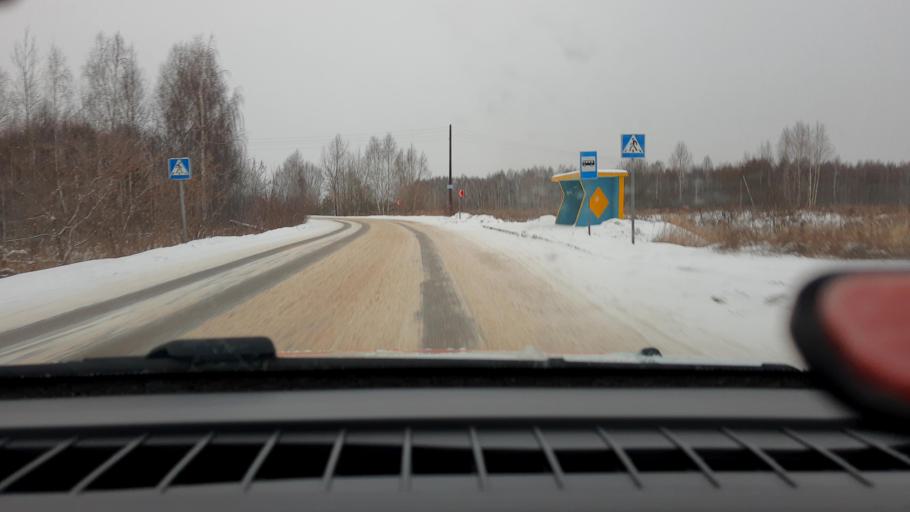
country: RU
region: Nizjnij Novgorod
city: Pamyat' Parizhskoy Kommuny
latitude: 56.2476
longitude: 44.4912
